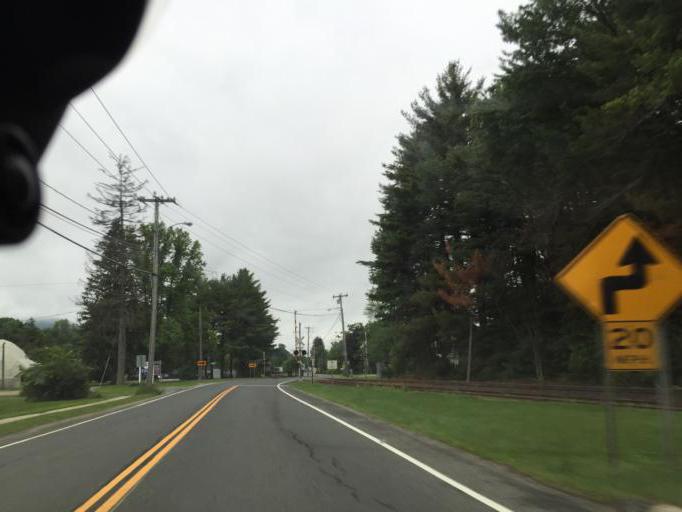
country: US
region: Connecticut
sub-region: Litchfield County
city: Canaan
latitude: 42.0335
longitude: -73.3271
